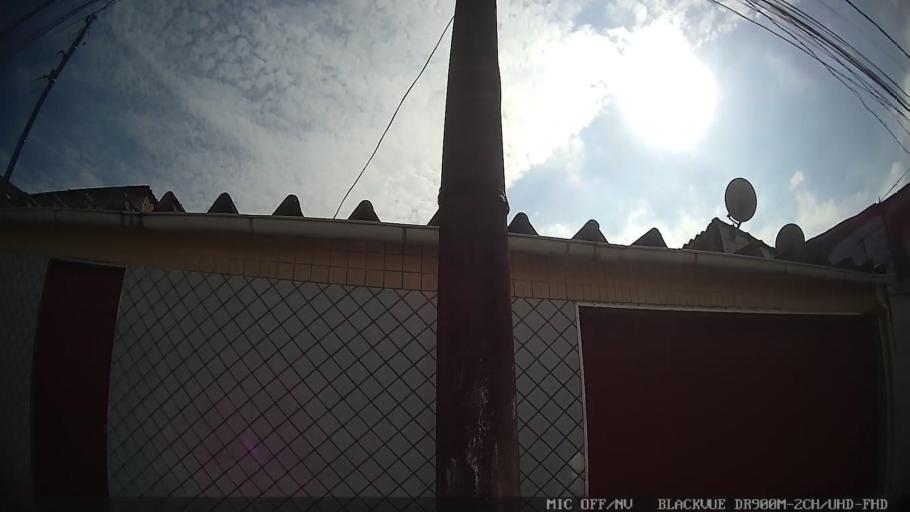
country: BR
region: Sao Paulo
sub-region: Santos
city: Santos
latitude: -23.9452
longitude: -46.3012
